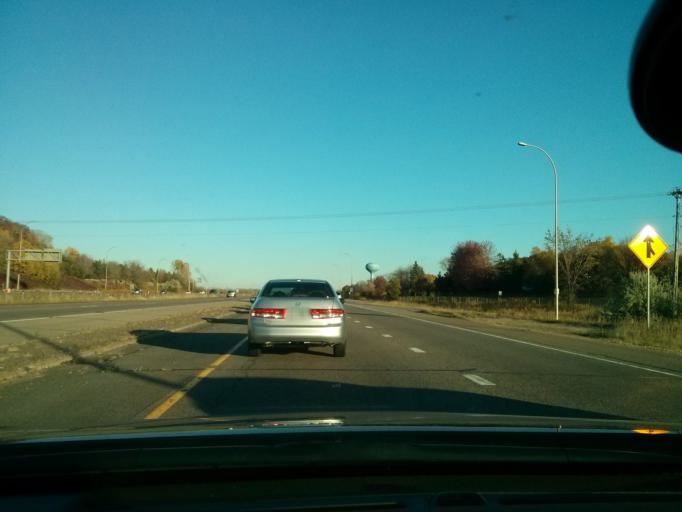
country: US
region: Minnesota
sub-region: Hennepin County
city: Edina
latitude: 44.8904
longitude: -93.3968
